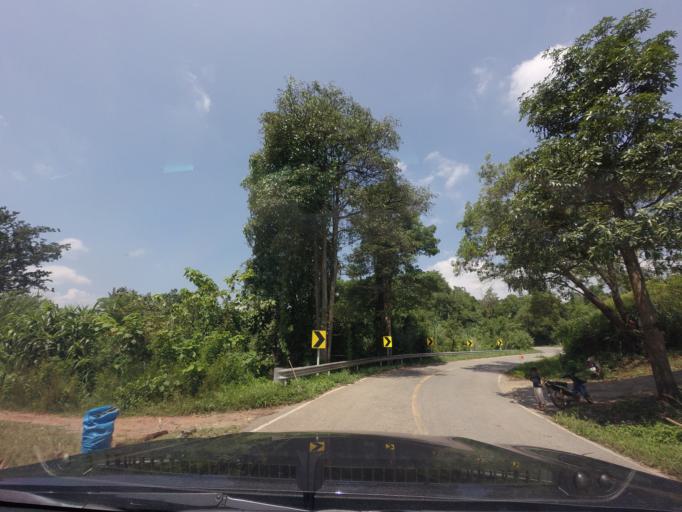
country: TH
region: Loei
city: Na Haeo
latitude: 17.6047
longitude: 100.8938
